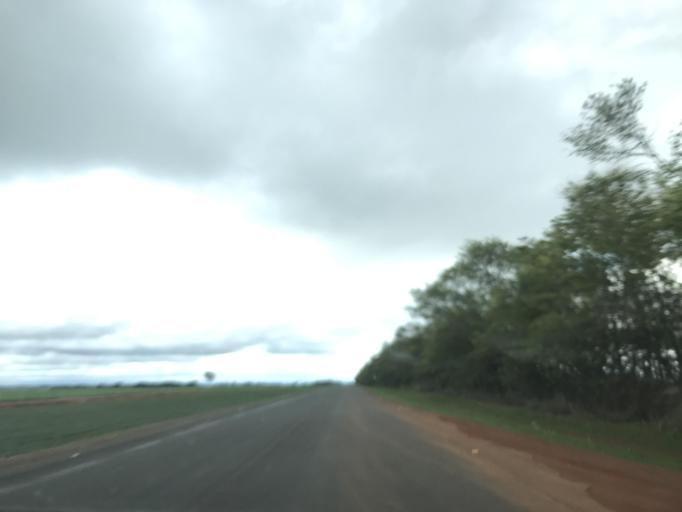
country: BR
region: Goias
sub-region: Vianopolis
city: Vianopolis
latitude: -16.7954
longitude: -48.5206
